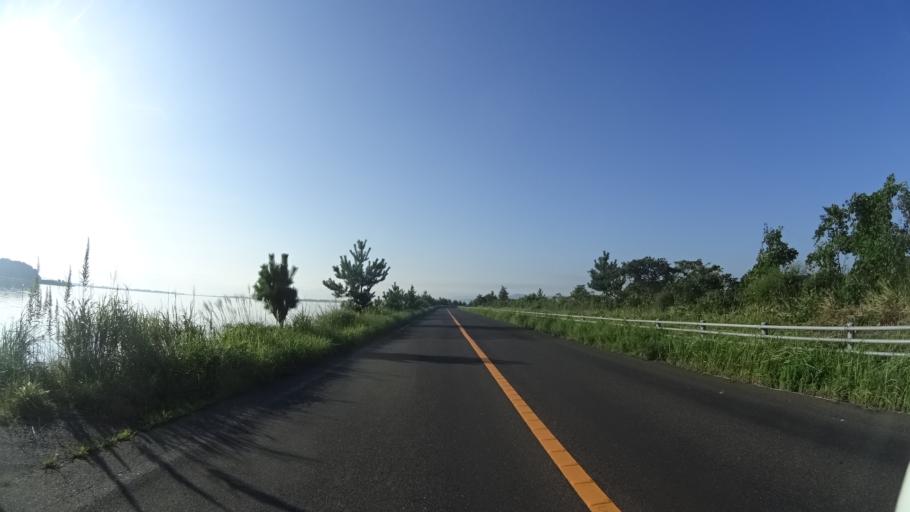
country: JP
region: Shimane
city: Sakaiminato
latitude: 35.5342
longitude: 133.1538
